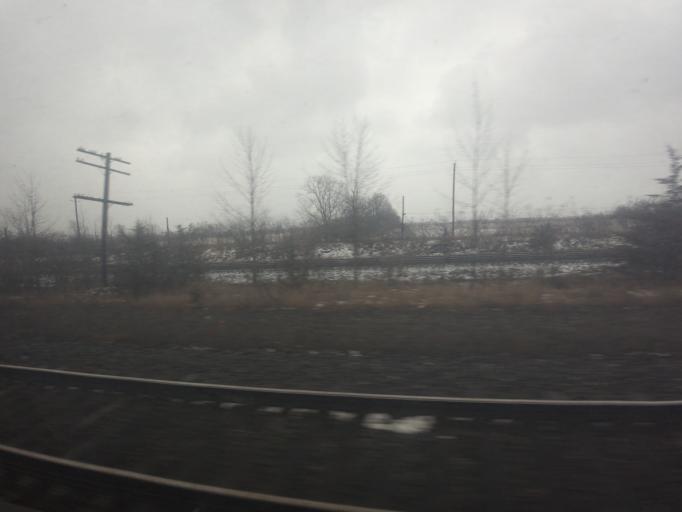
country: CA
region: Ontario
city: Quinte West
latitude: 44.0440
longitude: -77.7137
